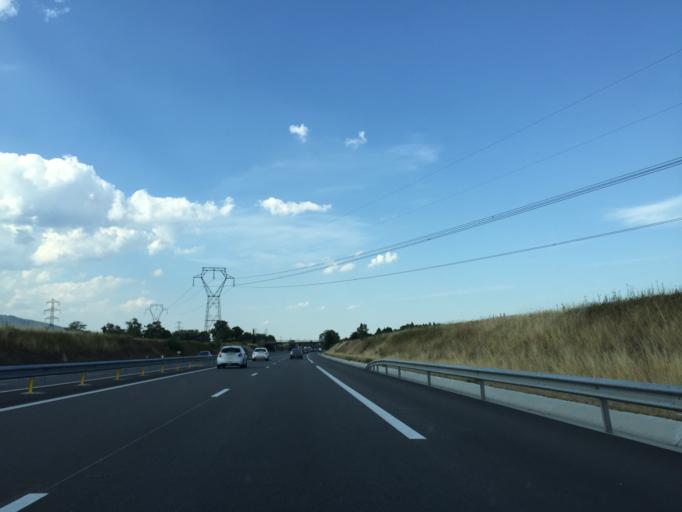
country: FR
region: Alsace
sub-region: Departement du Bas-Rhin
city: Kintzheim
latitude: 48.2519
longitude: 7.4120
